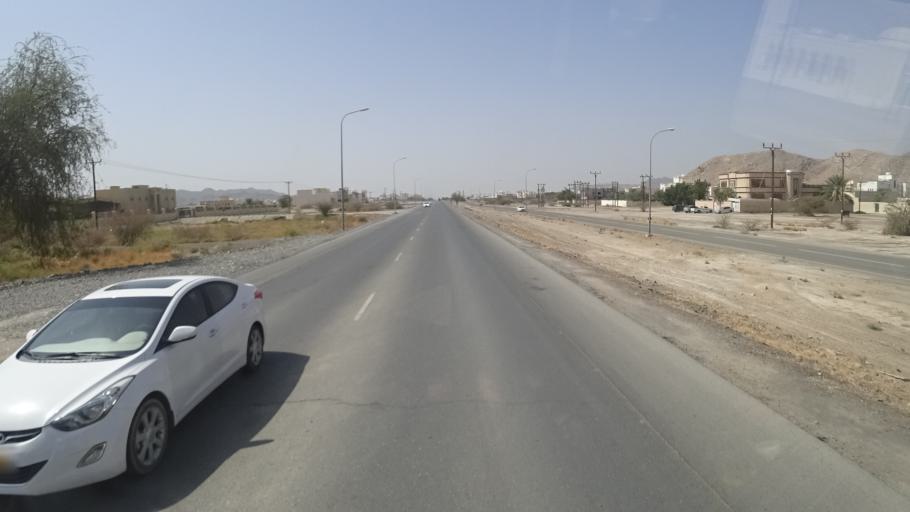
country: OM
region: Muhafazat ad Dakhiliyah
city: Bahla'
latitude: 23.0125
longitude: 57.3254
